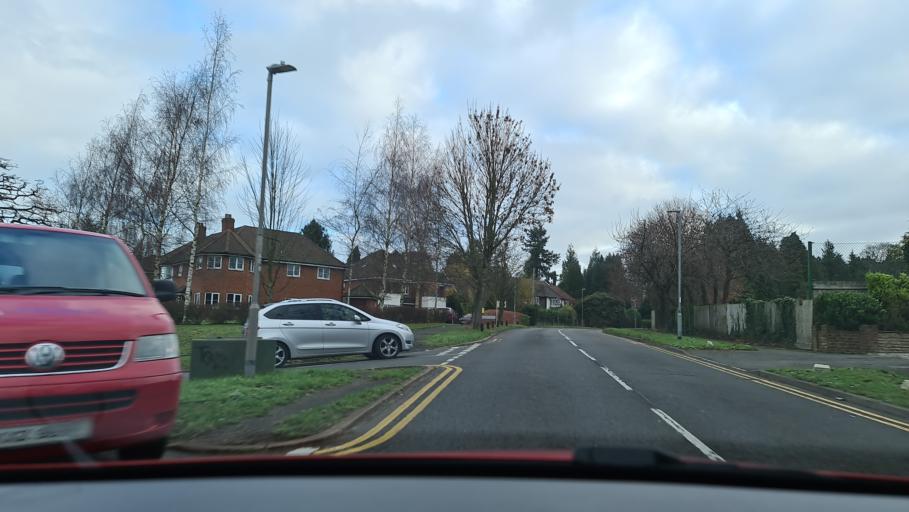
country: GB
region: England
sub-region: Buckinghamshire
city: High Wycombe
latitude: 51.6405
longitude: -0.7413
